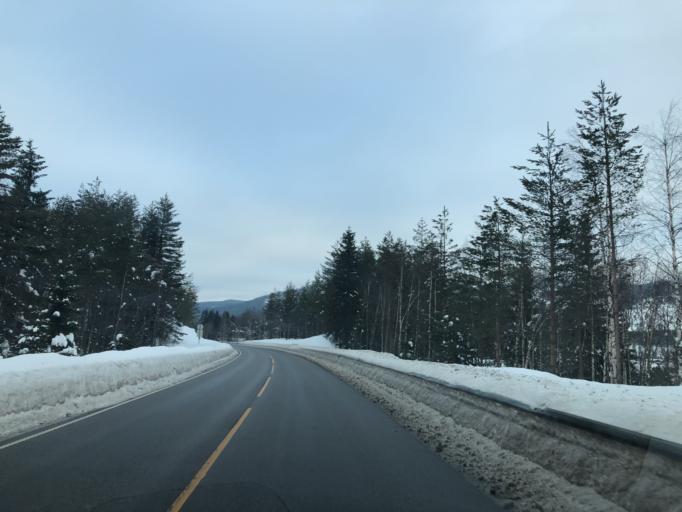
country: NO
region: Hedmark
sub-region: Trysil
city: Innbygda
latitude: 61.2630
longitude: 12.3084
